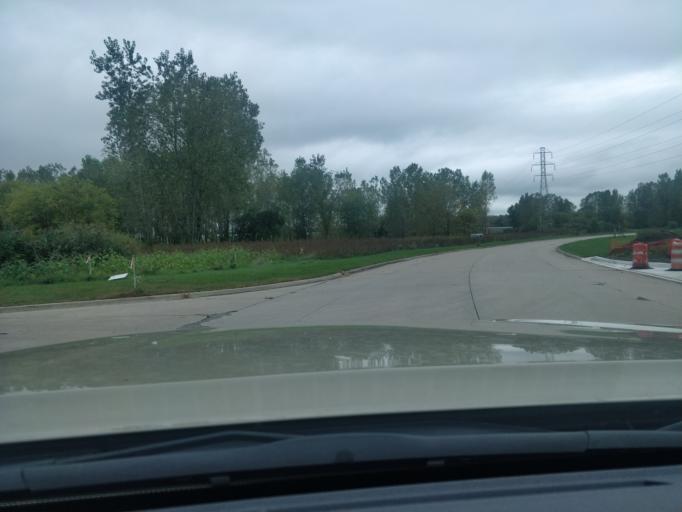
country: US
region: Michigan
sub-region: Wayne County
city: Romulus
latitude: 42.1764
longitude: -83.3907
